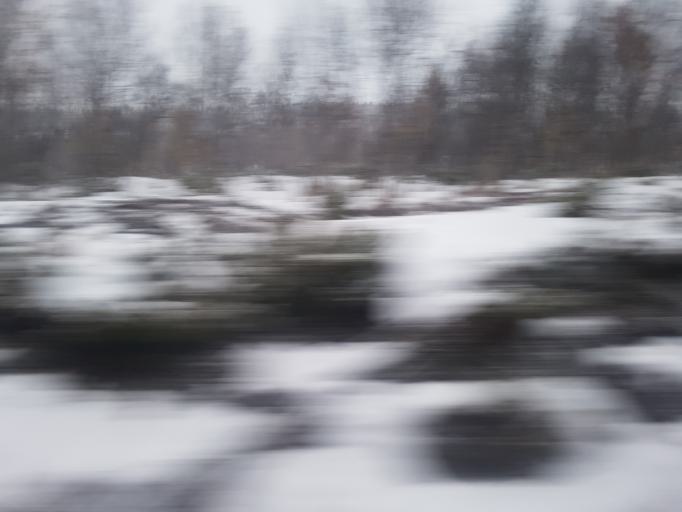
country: NO
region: Oppland
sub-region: Dovre
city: Dovre
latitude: 62.1758
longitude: 9.4499
